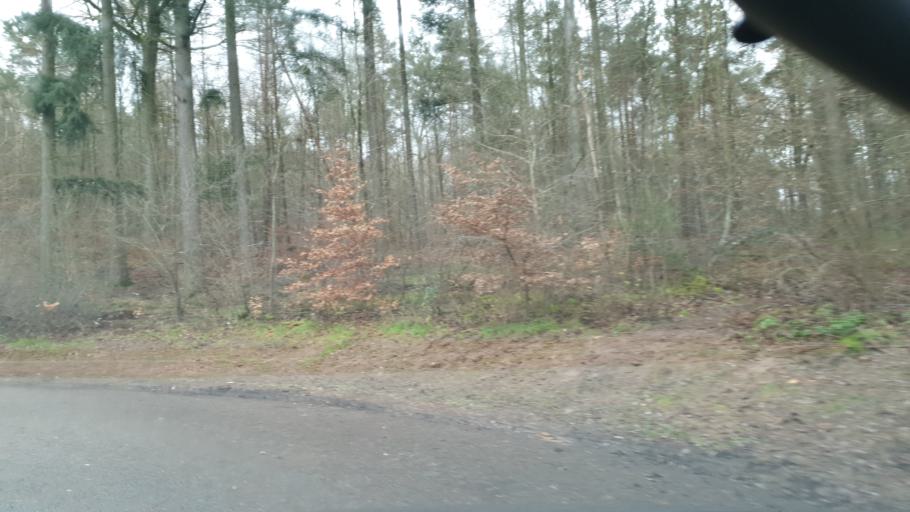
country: DE
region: Rheinland-Pfalz
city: Kaiserslautern
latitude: 49.4245
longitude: 7.7734
